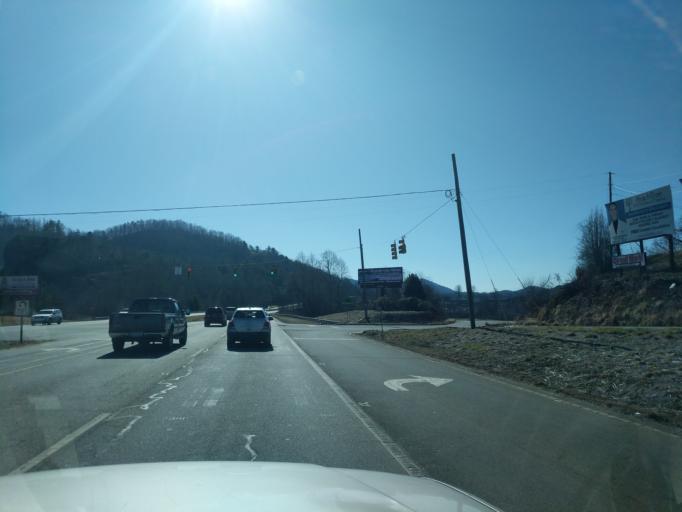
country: US
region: North Carolina
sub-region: Cherokee County
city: Murphy
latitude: 35.1063
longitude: -84.0095
